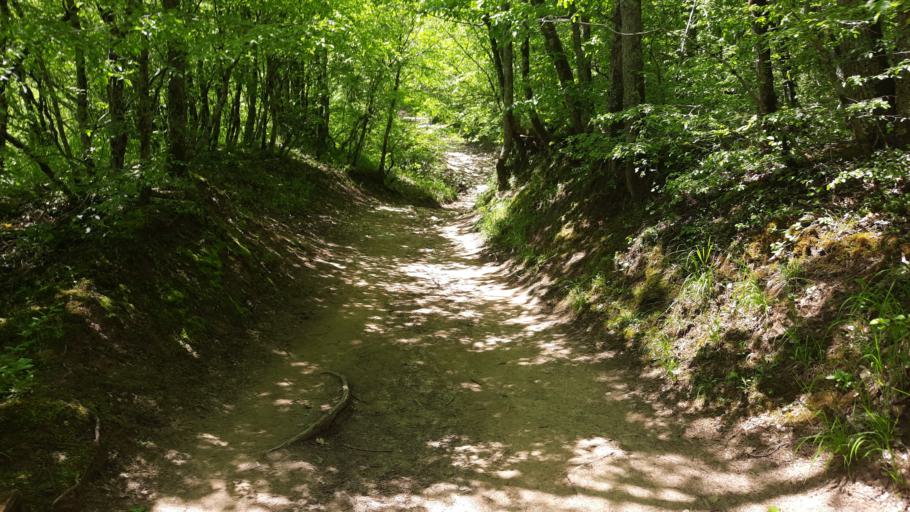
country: RU
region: Krasnodarskiy
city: Divnomorskoye
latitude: 44.5546
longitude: 38.2511
